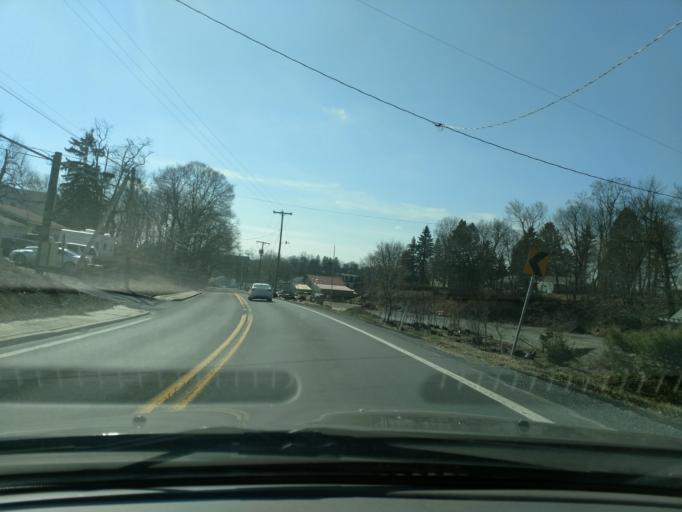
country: US
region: Pennsylvania
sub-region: Lebanon County
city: Sand Hill
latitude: 40.3567
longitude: -76.4236
